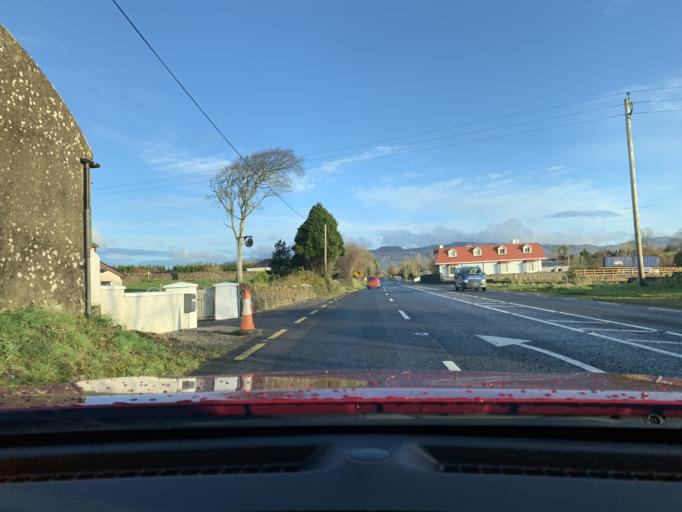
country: IE
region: Connaught
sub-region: Sligo
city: Sligo
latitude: 54.2926
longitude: -8.4738
